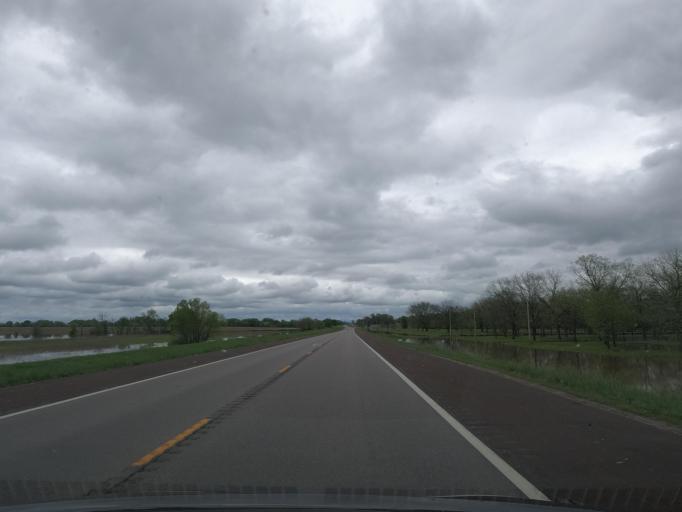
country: US
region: Kansas
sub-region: Labette County
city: Parsons
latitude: 37.3401
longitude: -95.1041
